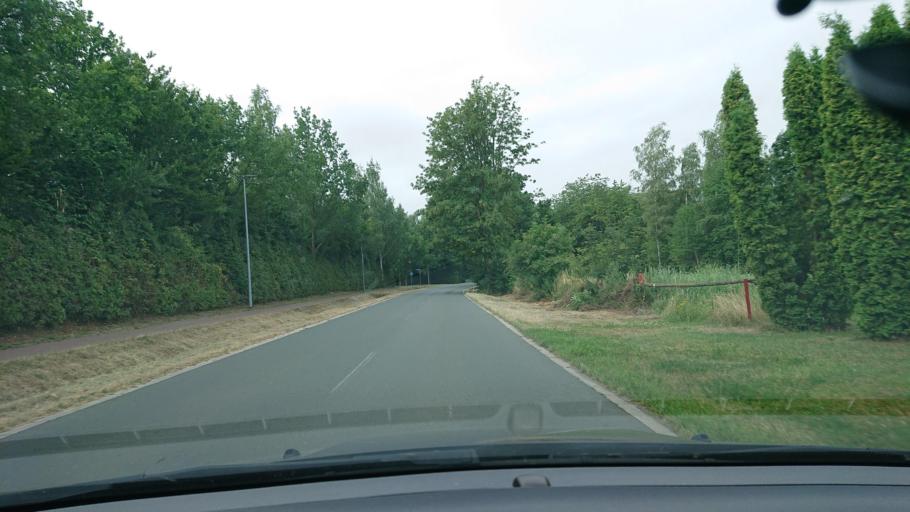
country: DE
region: North Rhine-Westphalia
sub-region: Regierungsbezirk Arnsberg
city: Soest
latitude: 51.5585
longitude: 8.0894
